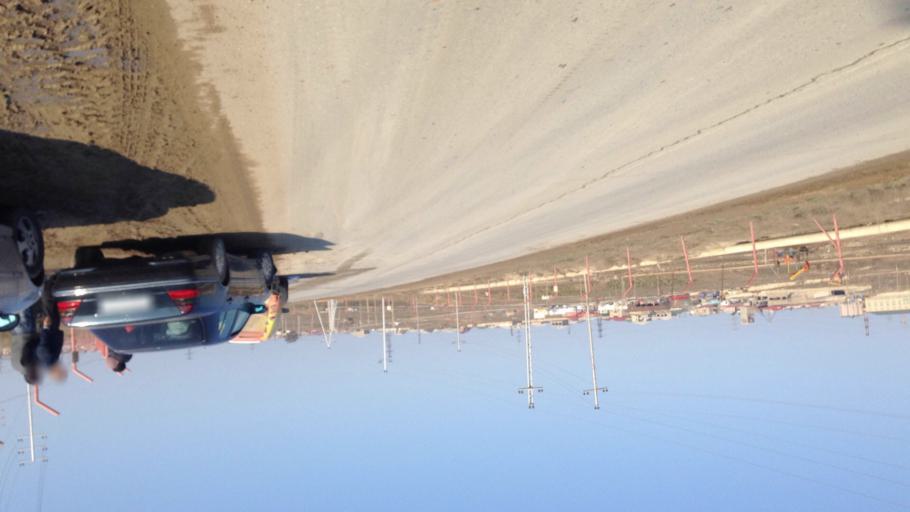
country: AZ
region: Abseron
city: Digah
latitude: 40.4762
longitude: 49.8537
